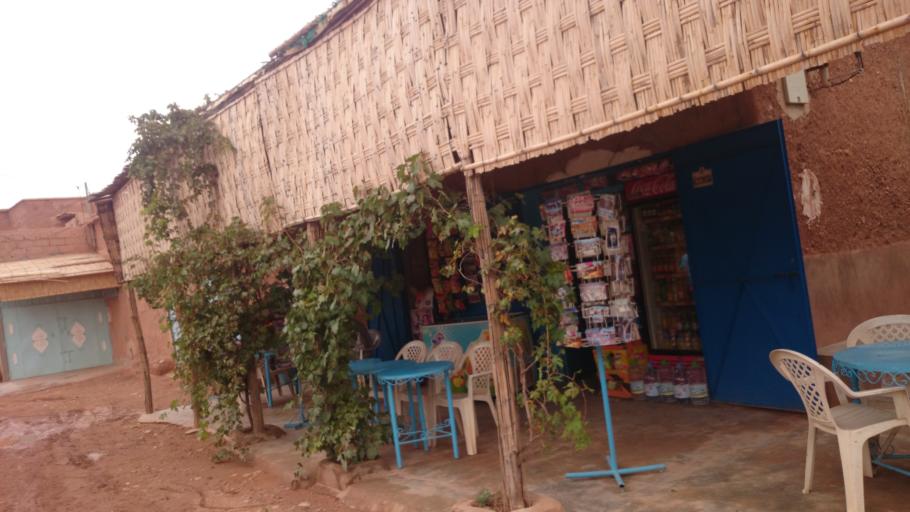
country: MA
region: Souss-Massa-Draa
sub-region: Ouarzazate
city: Amerzgane
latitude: 31.0448
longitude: -7.1321
